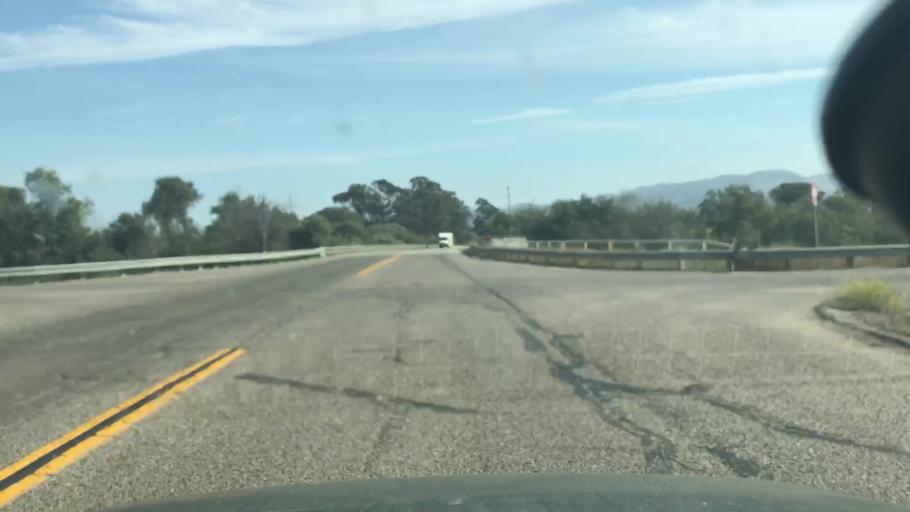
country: US
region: California
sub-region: Santa Barbara County
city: Vandenberg Village
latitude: 34.6734
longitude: -120.4936
